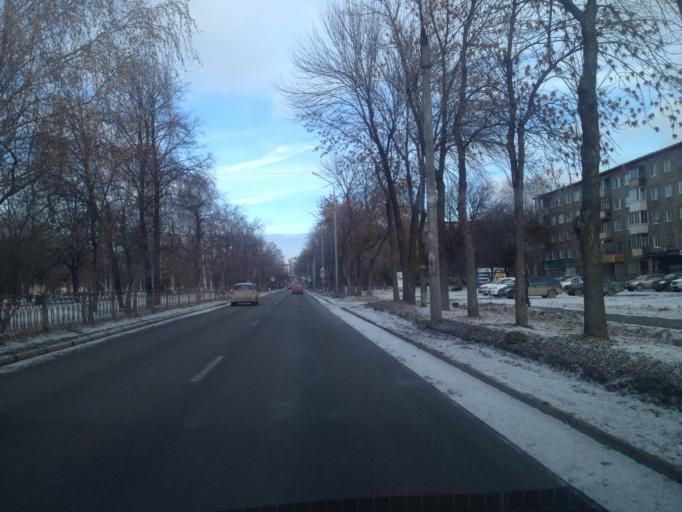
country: RU
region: Sverdlovsk
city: Yekaterinburg
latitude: 56.8192
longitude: 60.5811
